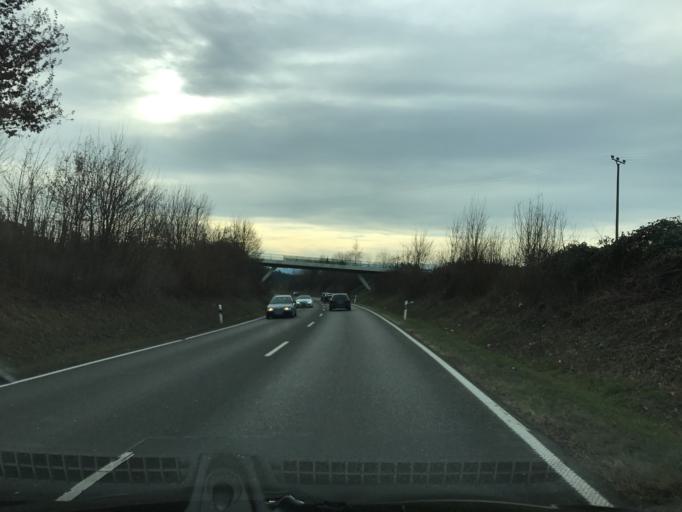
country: DE
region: Bavaria
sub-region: Swabia
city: Nonnenhorn
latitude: 47.5978
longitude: 9.6309
